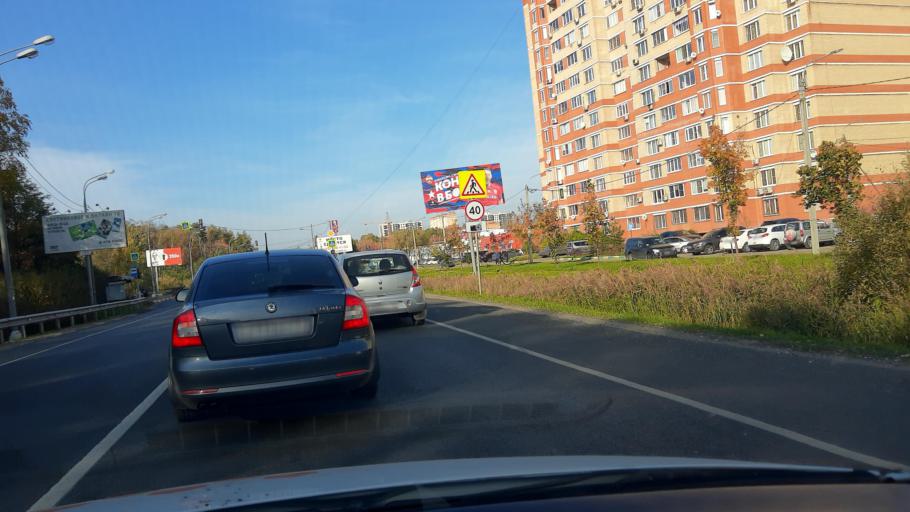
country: RU
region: Moskovskaya
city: Elektrostal'
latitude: 55.8024
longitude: 38.4284
